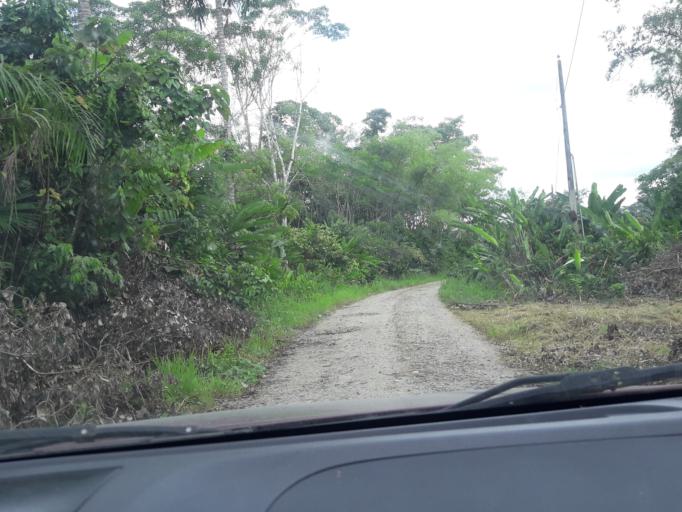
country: EC
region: Napo
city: Tena
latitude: -1.0962
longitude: -77.6769
